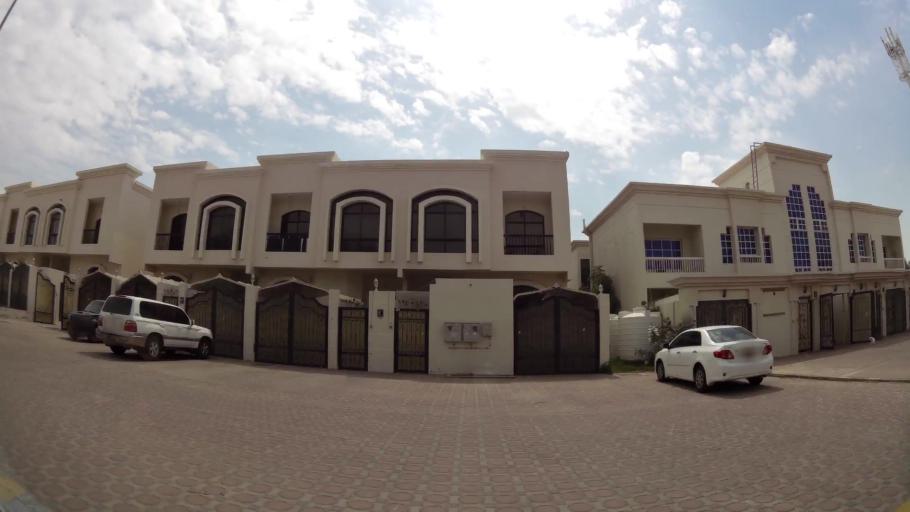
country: AE
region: Abu Dhabi
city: Al Ain
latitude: 24.2122
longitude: 55.7860
